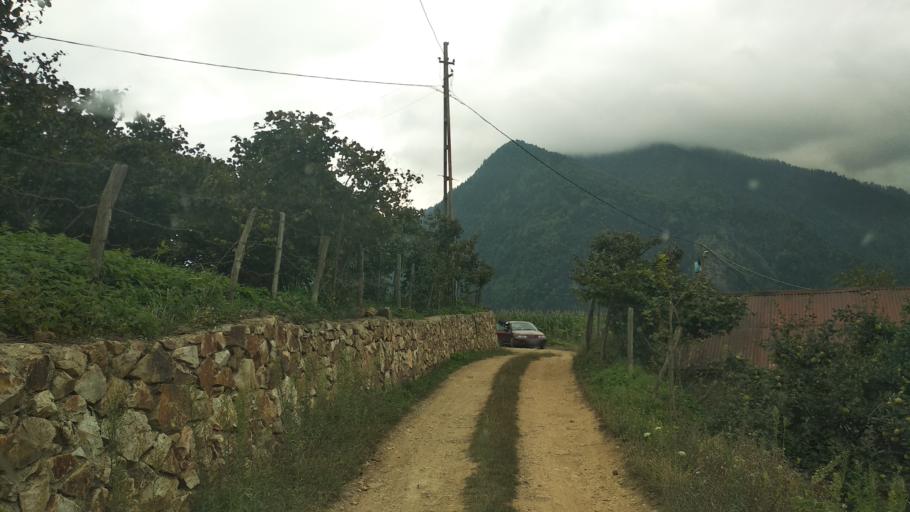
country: TR
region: Giresun
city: Dogankent
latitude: 40.7423
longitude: 38.9964
